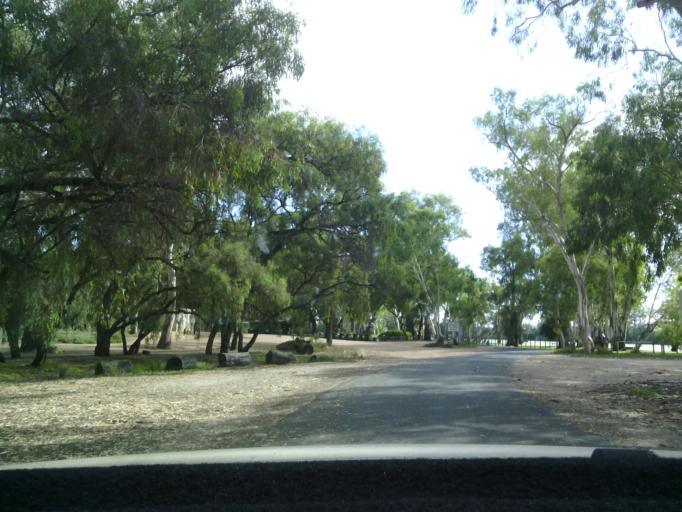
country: AU
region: South Australia
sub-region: Berri and Barmera
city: Berri
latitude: -34.2899
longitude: 140.6307
